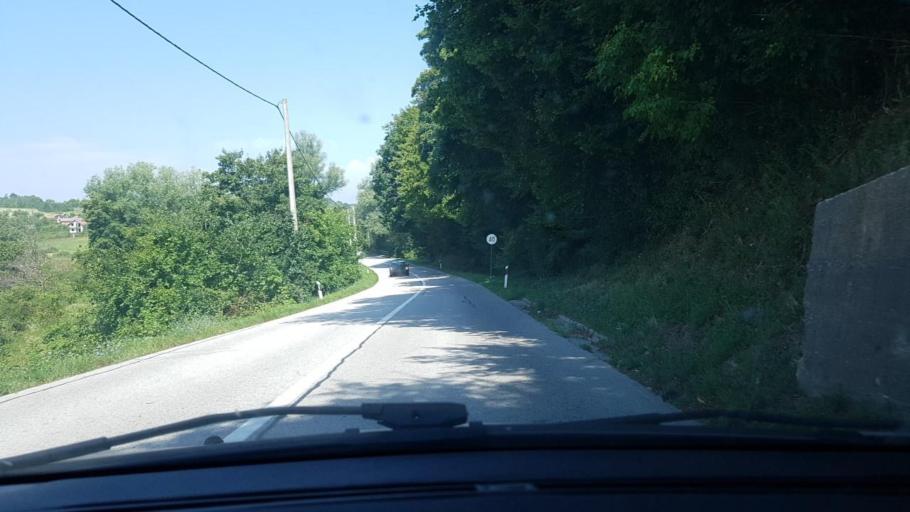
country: BA
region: Federation of Bosnia and Herzegovina
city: Velika Kladusa
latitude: 45.2144
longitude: 15.7364
